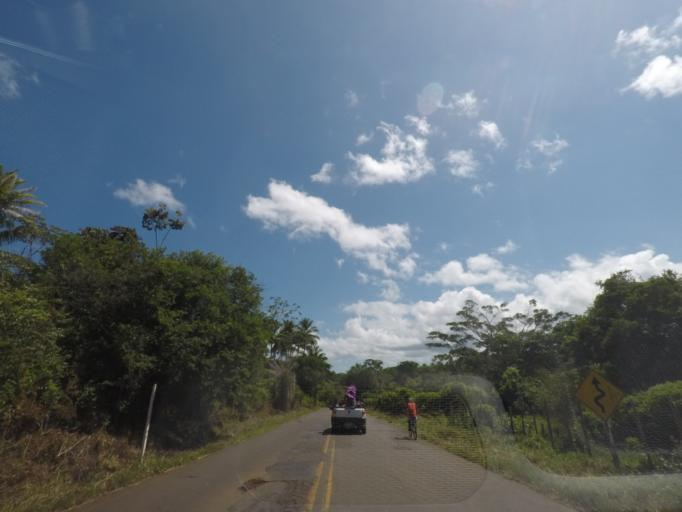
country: BR
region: Bahia
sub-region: Taperoa
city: Taperoa
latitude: -13.5055
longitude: -39.0938
